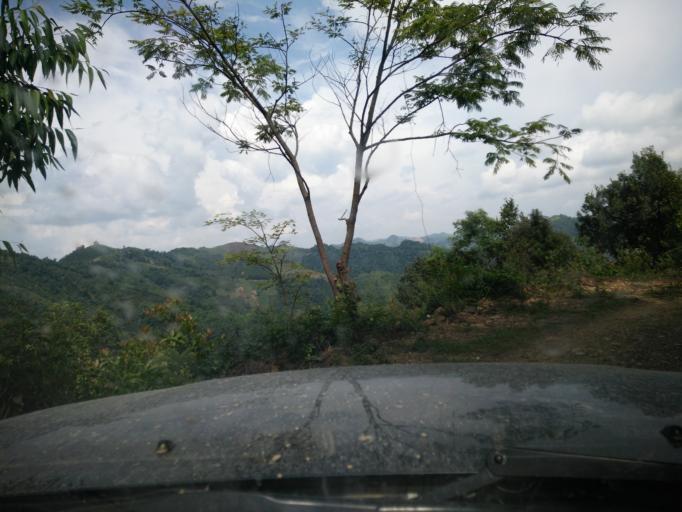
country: CN
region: Guangxi Zhuangzu Zizhiqu
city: Leli
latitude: 24.7683
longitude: 105.9043
